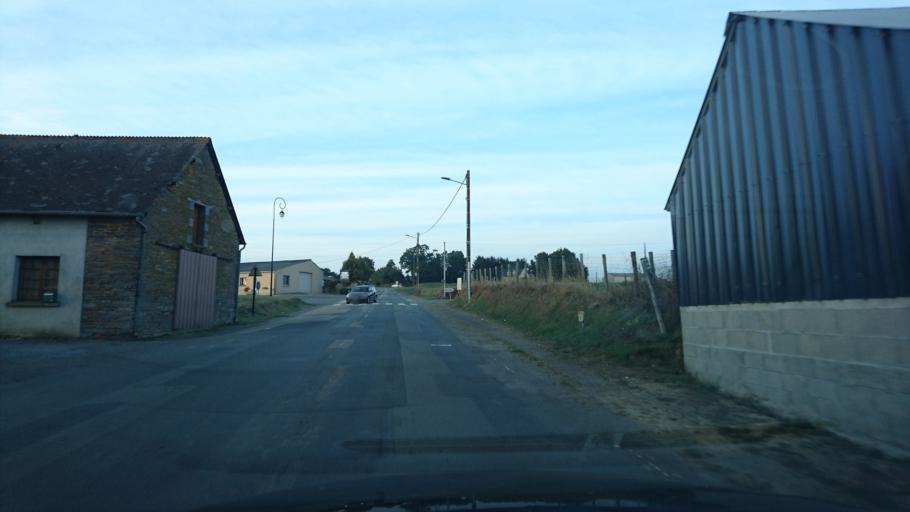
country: FR
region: Brittany
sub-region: Departement d'Ille-et-Vilaine
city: Sixt-sur-Aff
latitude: 47.8153
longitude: -2.0197
